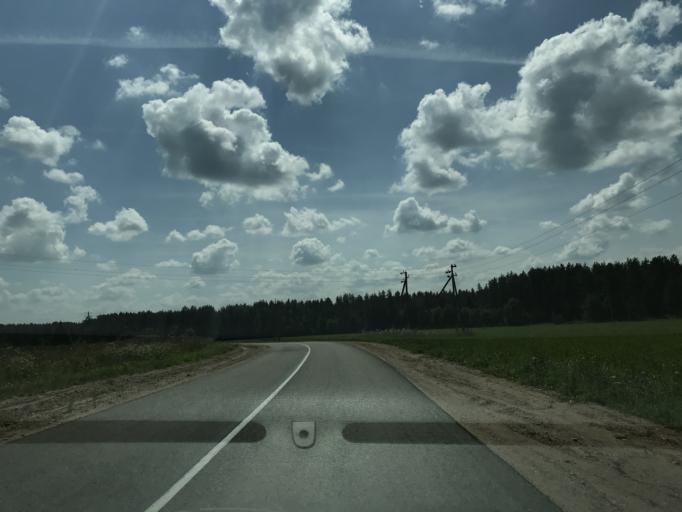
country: BY
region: Minsk
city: Rakaw
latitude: 54.0090
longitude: 26.9810
